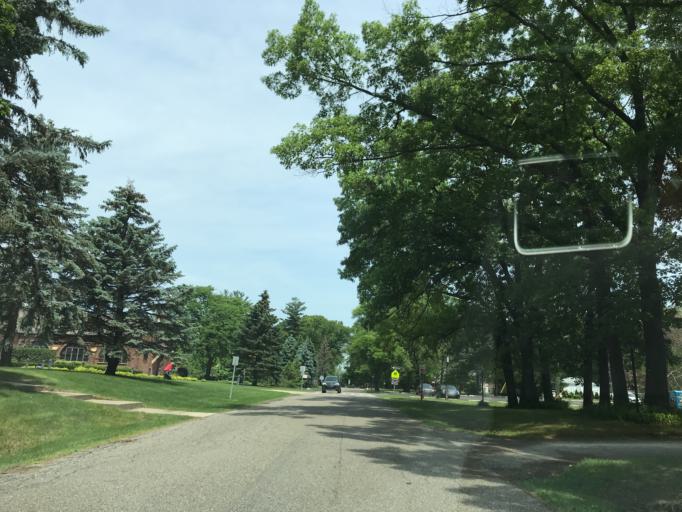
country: US
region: Michigan
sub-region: Oakland County
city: Southfield
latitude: 42.4729
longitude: -83.2654
